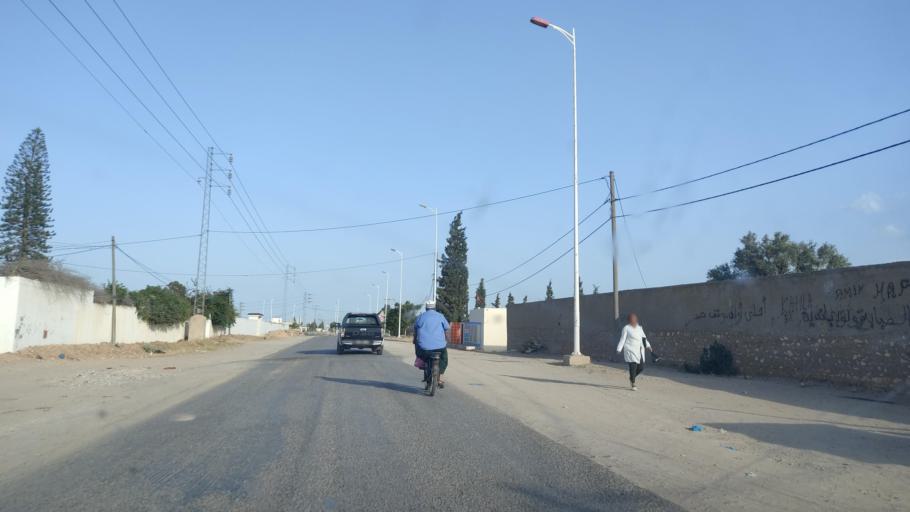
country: TN
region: Safaqis
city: Sfax
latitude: 34.7984
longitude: 10.6769
